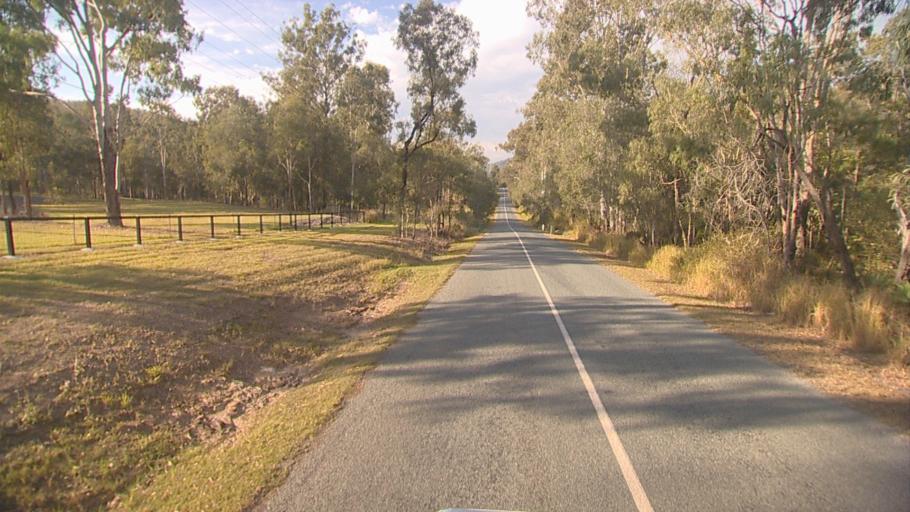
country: AU
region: Queensland
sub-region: Gold Coast
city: Ormeau Hills
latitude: -27.8411
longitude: 153.1626
